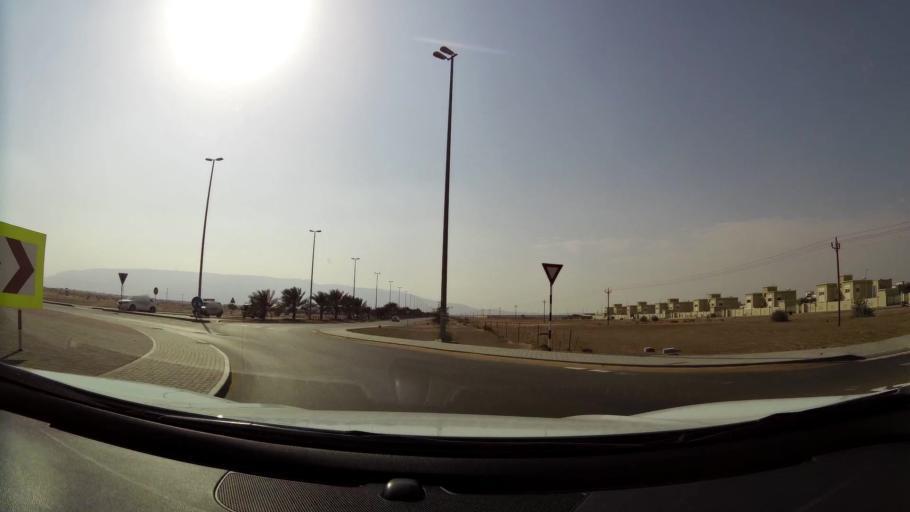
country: AE
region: Abu Dhabi
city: Al Ain
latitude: 24.0932
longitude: 55.8919
